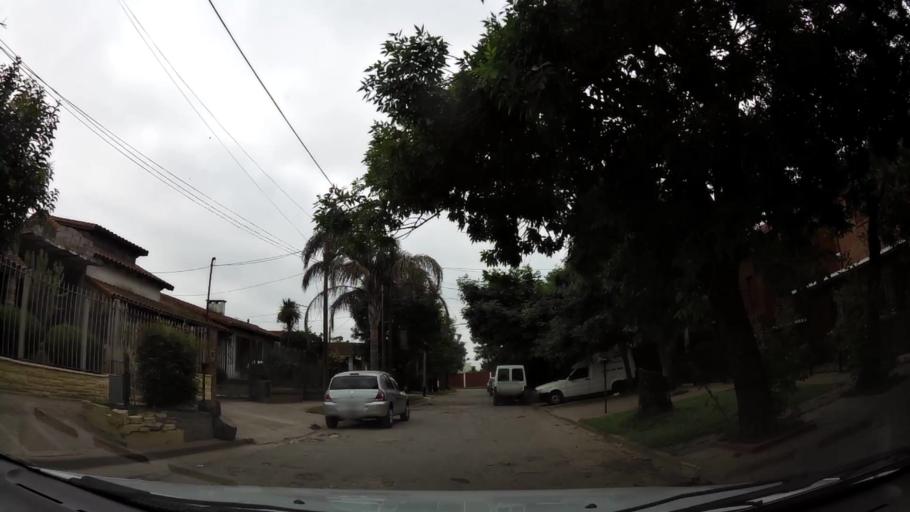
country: AR
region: Buenos Aires
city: San Justo
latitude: -34.7144
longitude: -58.5354
